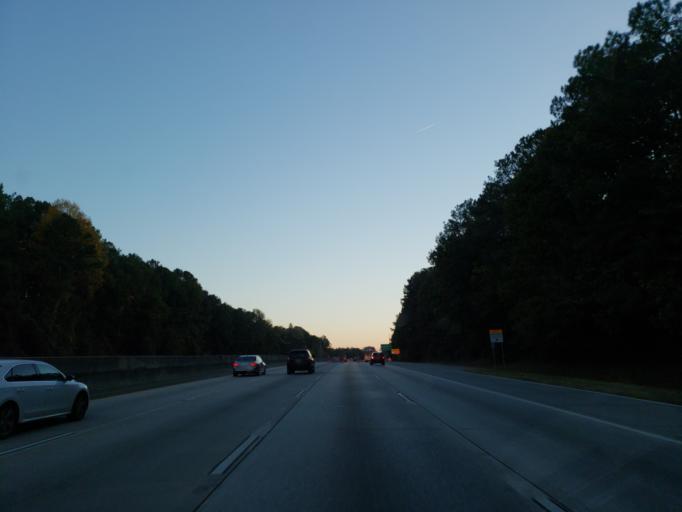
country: US
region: Georgia
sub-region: Fulton County
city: Roswell
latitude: 33.9969
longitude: -84.3363
